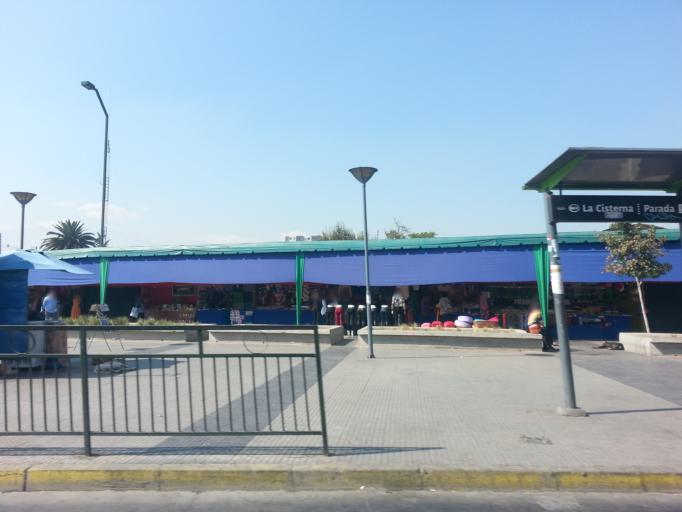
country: CL
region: Santiago Metropolitan
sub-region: Provincia de Santiago
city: La Pintana
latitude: -33.5394
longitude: -70.6647
